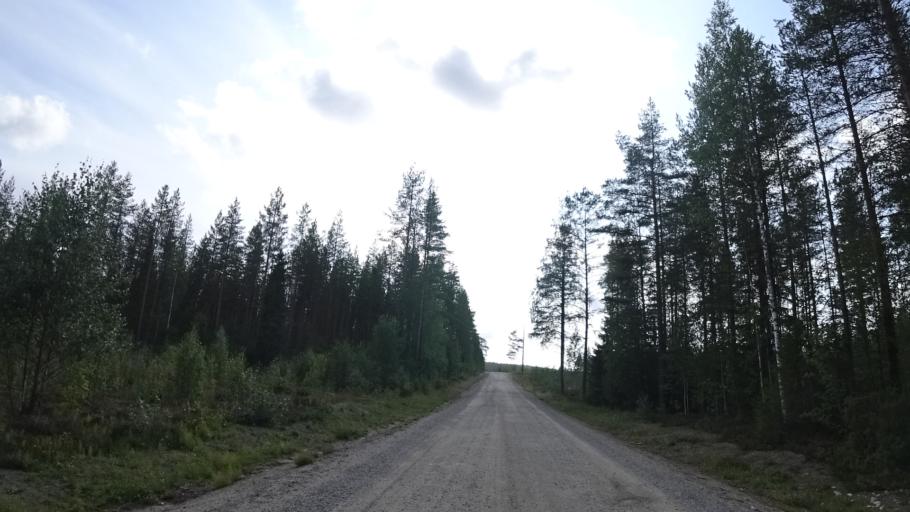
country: FI
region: North Karelia
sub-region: Pielisen Karjala
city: Lieksa
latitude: 63.5751
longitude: 30.1204
